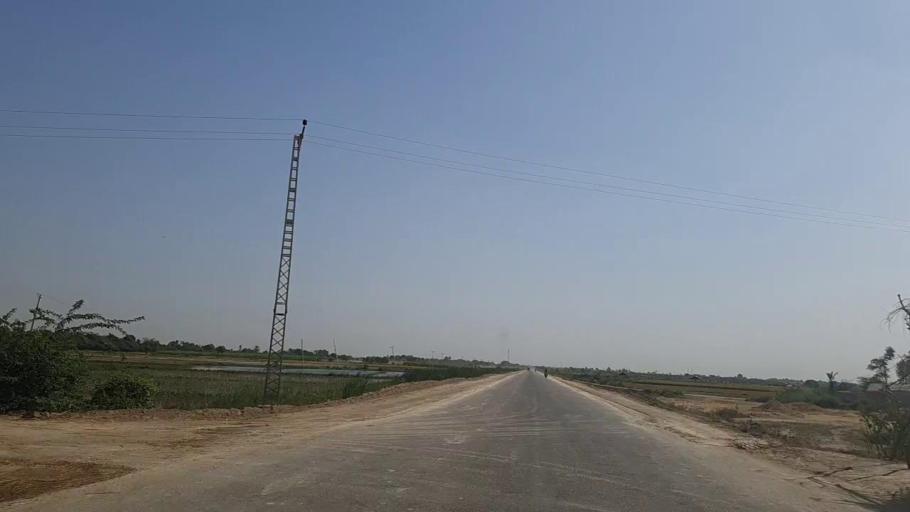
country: PK
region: Sindh
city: Mirpur Batoro
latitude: 24.7500
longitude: 68.2363
